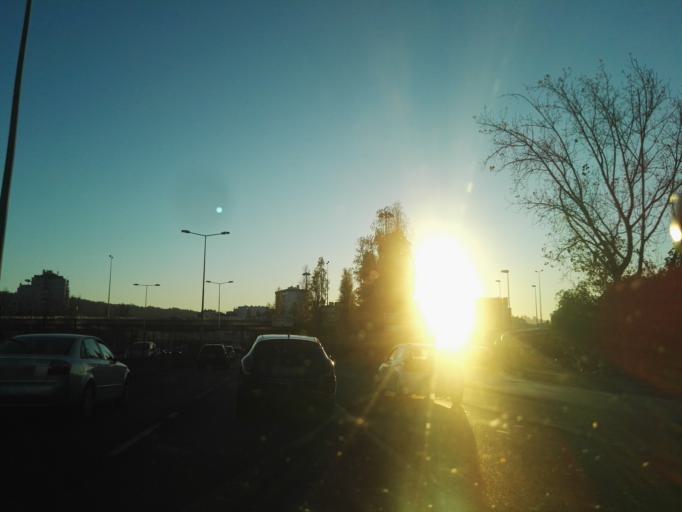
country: PT
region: Lisbon
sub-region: Odivelas
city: Pontinha
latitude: 38.7534
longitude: -9.1865
